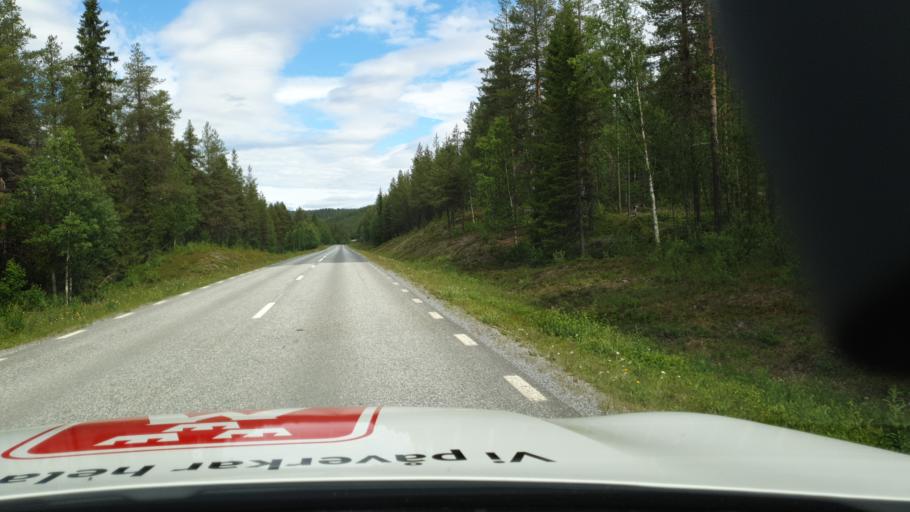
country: SE
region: Vaesterbotten
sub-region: Storumans Kommun
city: Fristad
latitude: 65.3726
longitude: 16.5171
